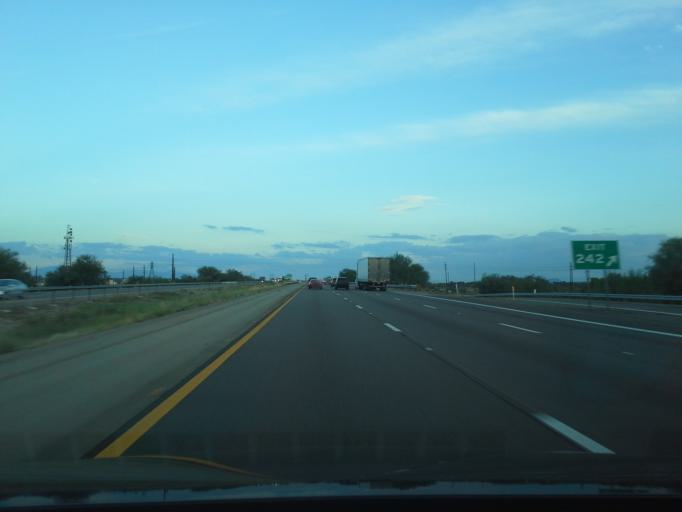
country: US
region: Arizona
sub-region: Pima County
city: Marana
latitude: 32.4026
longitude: -111.1333
